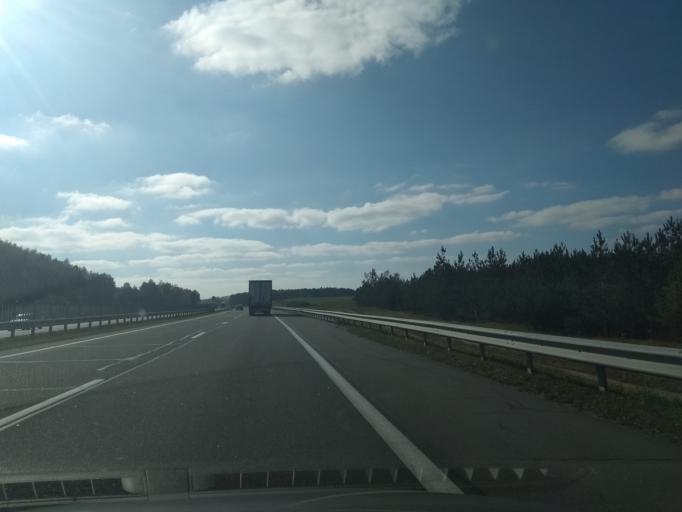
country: BY
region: Brest
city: Baranovichi
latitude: 53.1236
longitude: 25.9031
